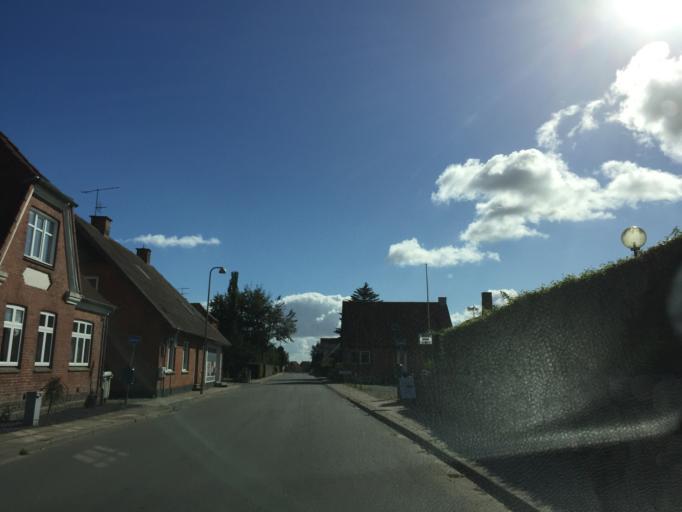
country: DK
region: Central Jutland
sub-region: Viborg Kommune
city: Bjerringbro
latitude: 56.4107
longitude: 9.6135
